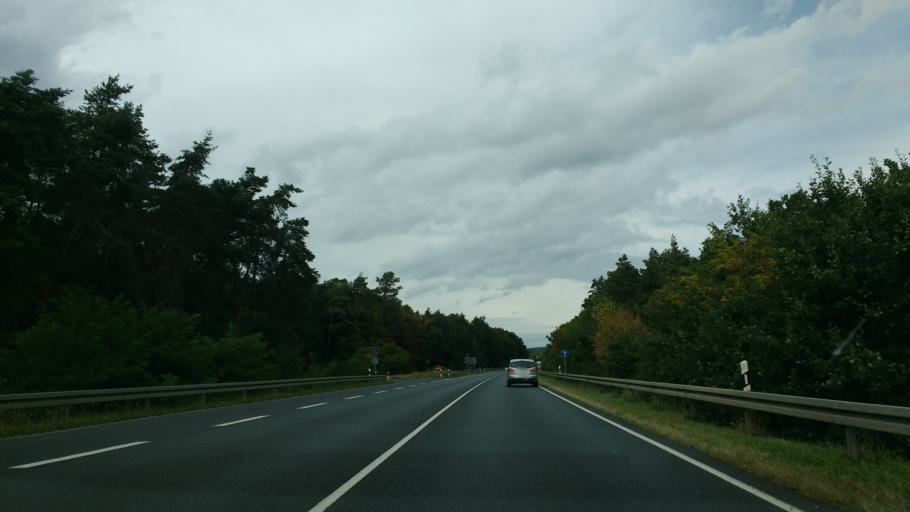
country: DE
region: Bavaria
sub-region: Regierungsbezirk Unterfranken
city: Schwebheim
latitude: 50.0155
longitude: 10.2379
